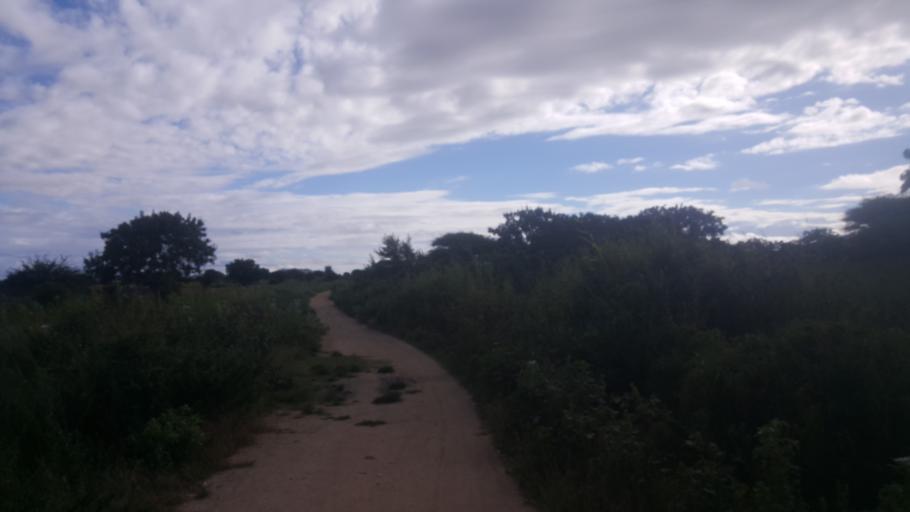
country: TZ
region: Dodoma
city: Dodoma
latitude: -6.0929
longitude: 35.5281
